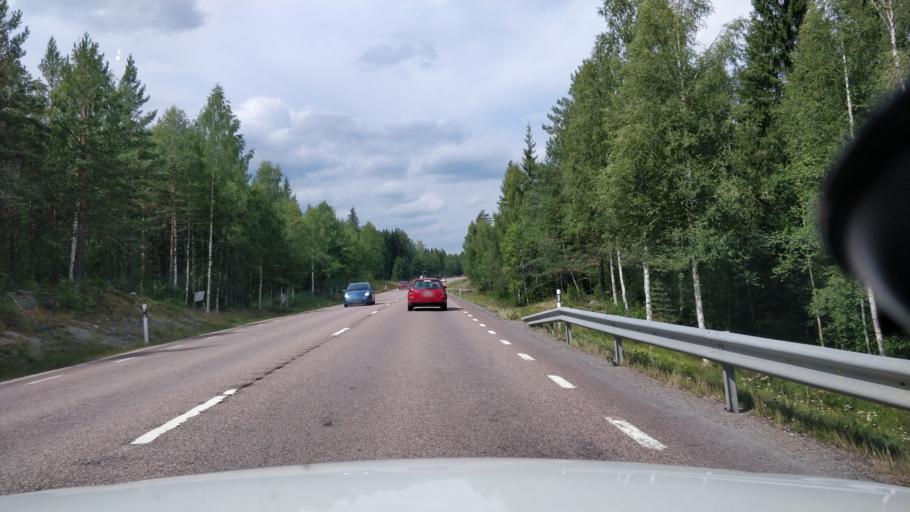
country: SE
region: Dalarna
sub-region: Faluns Kommun
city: Falun
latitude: 60.6402
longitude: 15.5804
